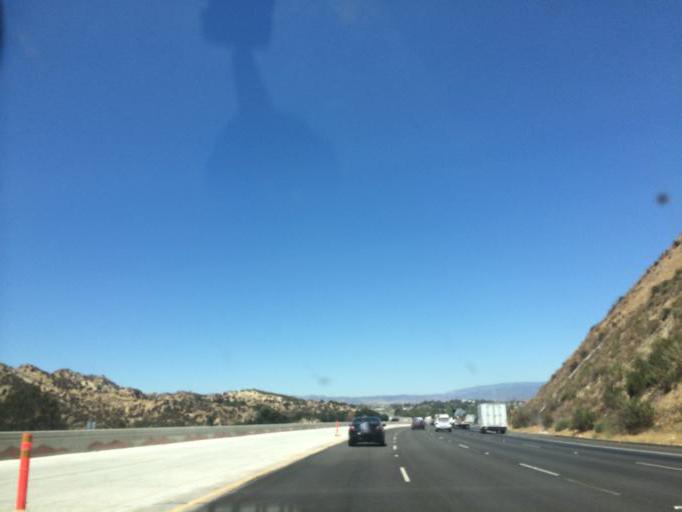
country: US
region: California
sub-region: Los Angeles County
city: Santa Clarita
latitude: 34.3585
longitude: -118.5536
